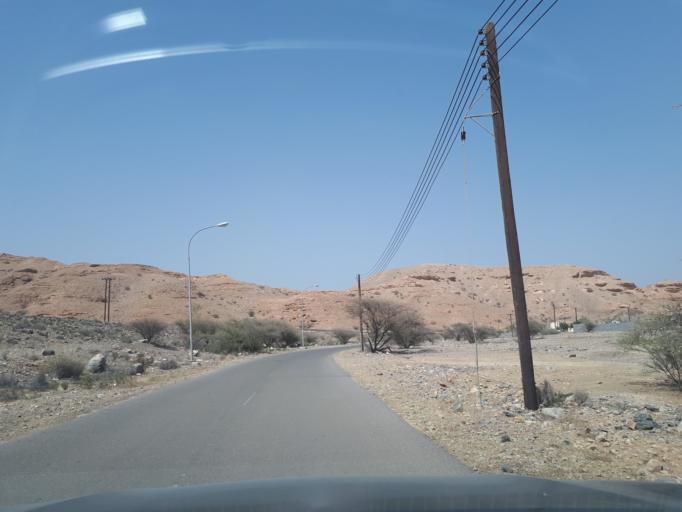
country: OM
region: Ash Sharqiyah
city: Ibra'
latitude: 23.0915
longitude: 58.8574
